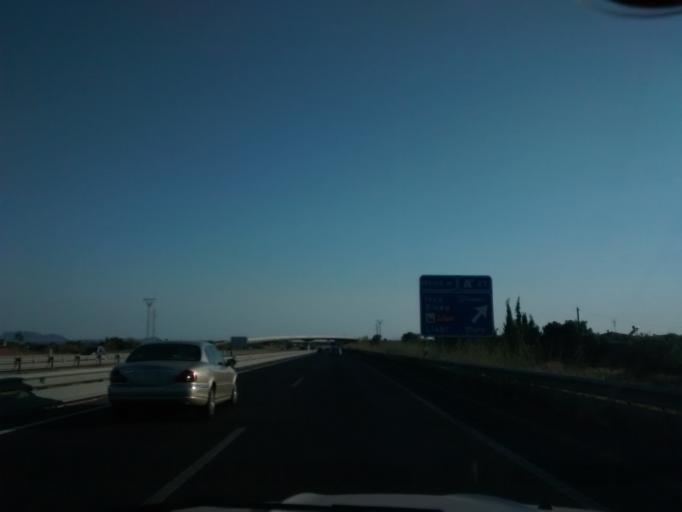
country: ES
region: Balearic Islands
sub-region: Illes Balears
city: Inca
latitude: 39.7266
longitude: 2.9318
